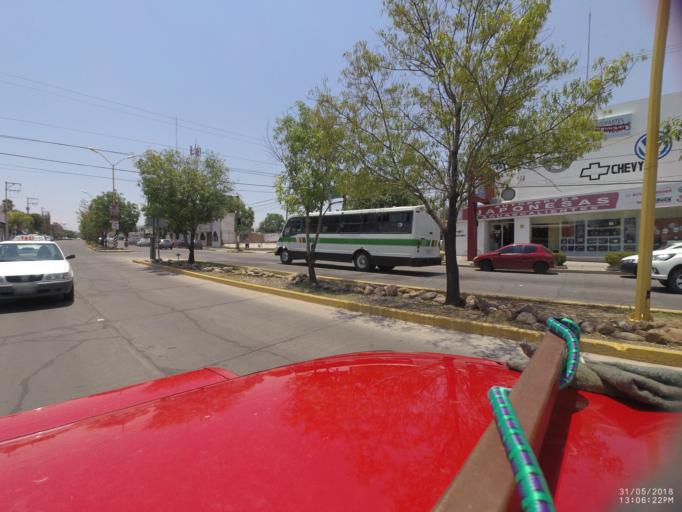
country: MX
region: Aguascalientes
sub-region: Aguascalientes
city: Aguascalientes
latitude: 21.8736
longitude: -102.2874
